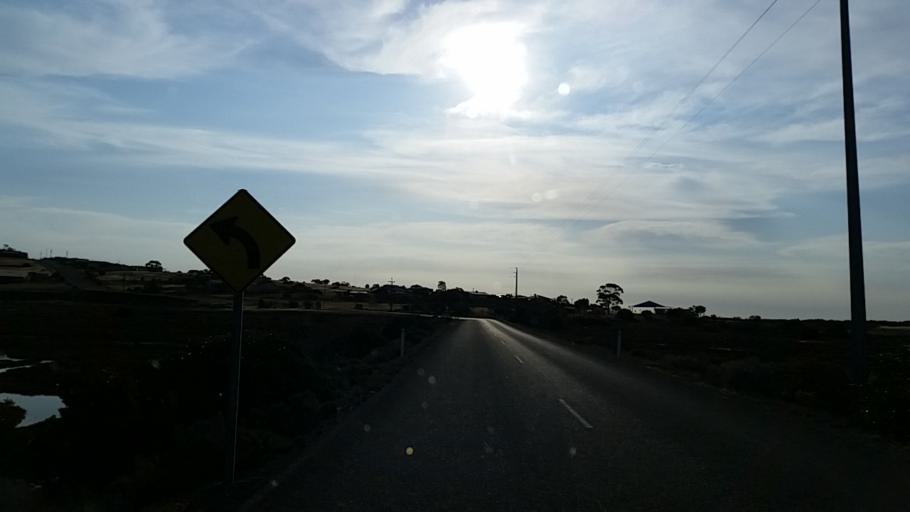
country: AU
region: South Australia
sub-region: Port Pirie City and Dists
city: Port Pirie
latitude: -33.1017
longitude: 138.0372
